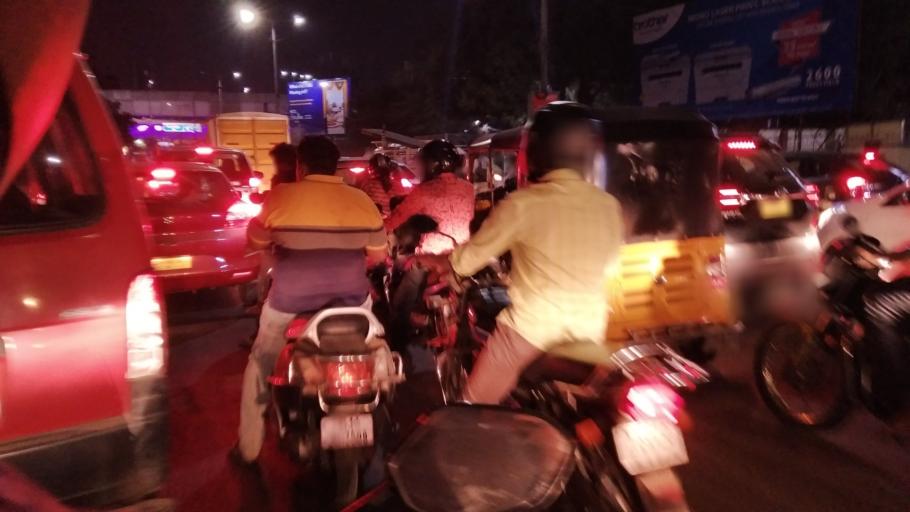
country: IN
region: Telangana
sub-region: Hyderabad
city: Malkajgiri
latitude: 17.4449
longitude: 78.4874
